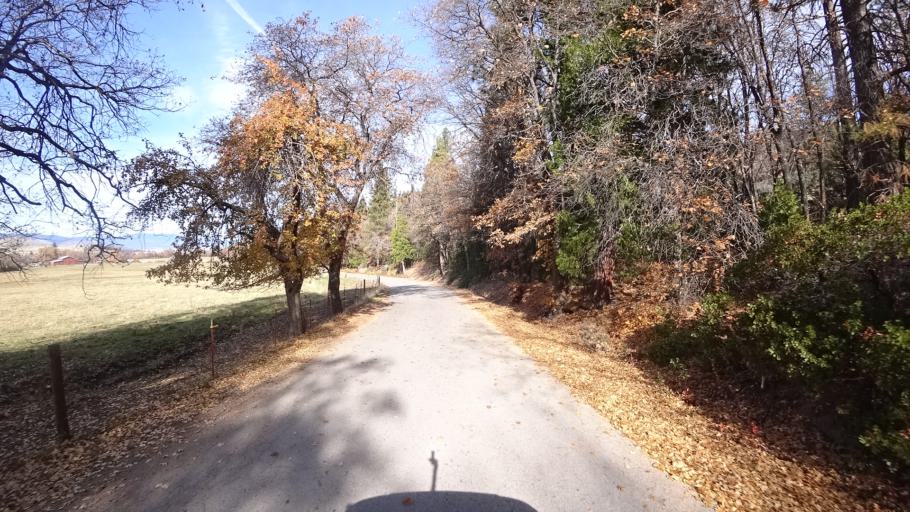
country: US
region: California
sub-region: Siskiyou County
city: Weed
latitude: 41.4441
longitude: -122.4239
